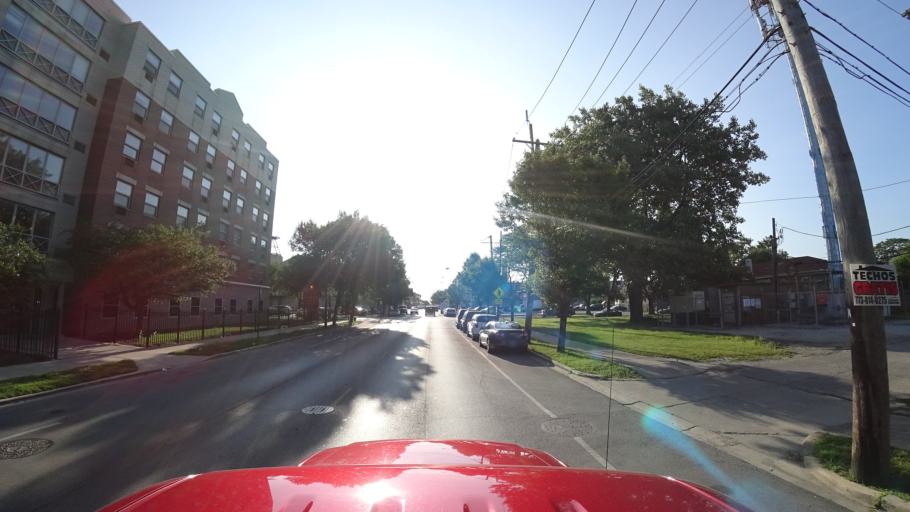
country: US
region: Illinois
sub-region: Cook County
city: Hometown
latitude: 41.7862
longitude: -87.7053
